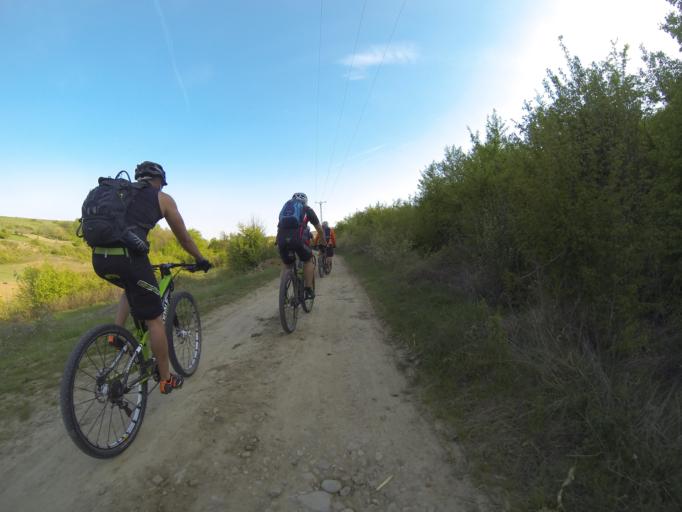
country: RO
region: Dolj
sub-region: Comuna Filiasi
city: Racarii de Sus
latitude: 44.5475
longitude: 23.5987
